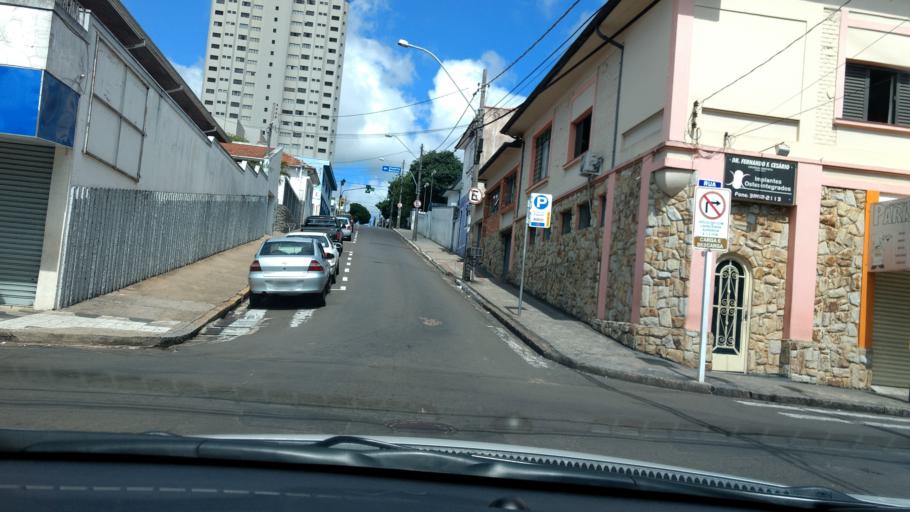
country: BR
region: Sao Paulo
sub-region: Botucatu
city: Botucatu
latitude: -22.8921
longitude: -48.4410
